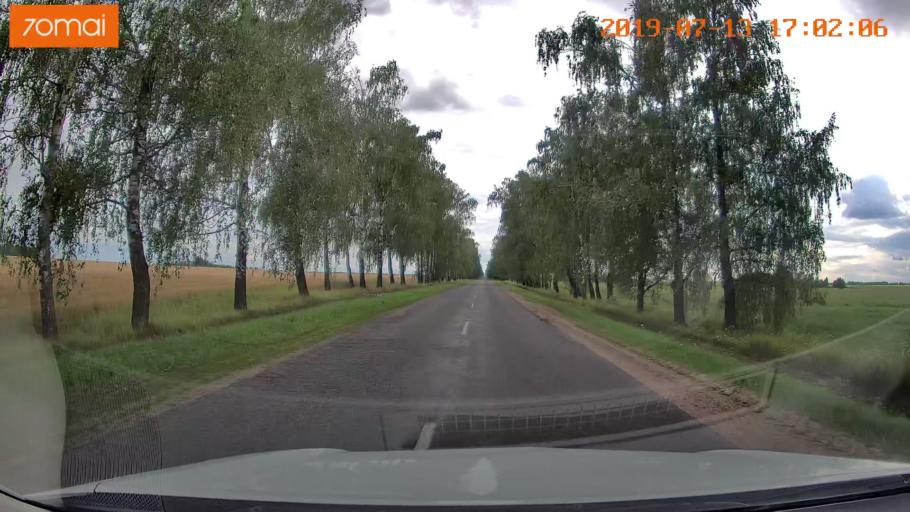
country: BY
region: Mogilev
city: Kirawsk
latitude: 53.2893
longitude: 29.3902
